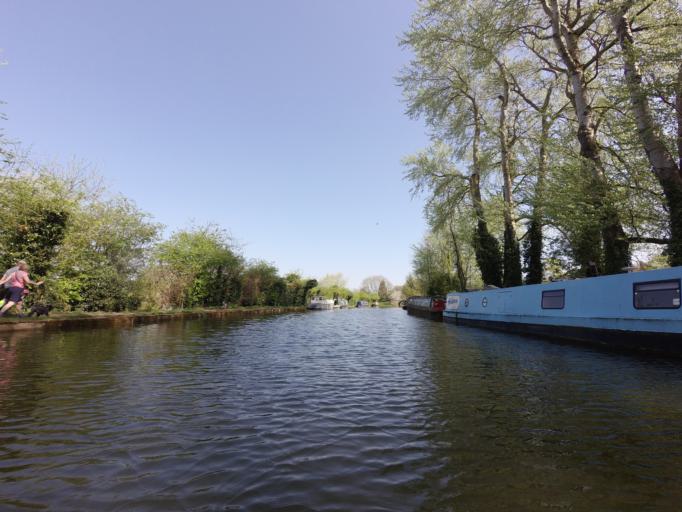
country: GB
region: England
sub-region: Buckinghamshire
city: Cheddington
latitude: 51.8227
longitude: -0.6692
